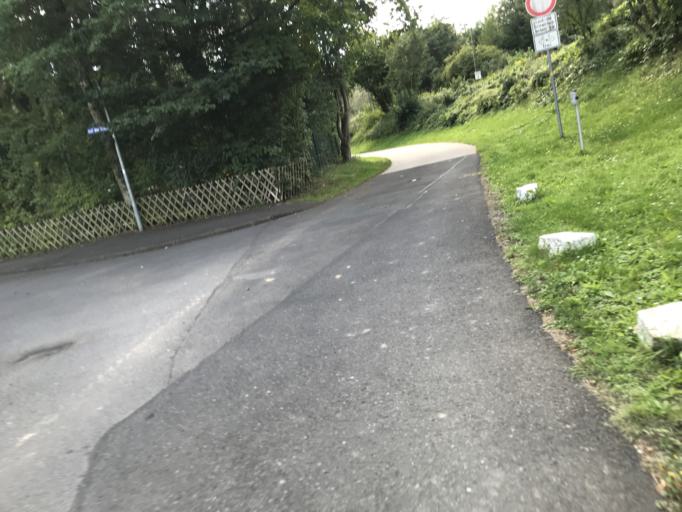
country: DE
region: Hesse
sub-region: Regierungsbezirk Kassel
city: Bad Sooden-Allendorf
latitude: 51.2249
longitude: 9.9905
